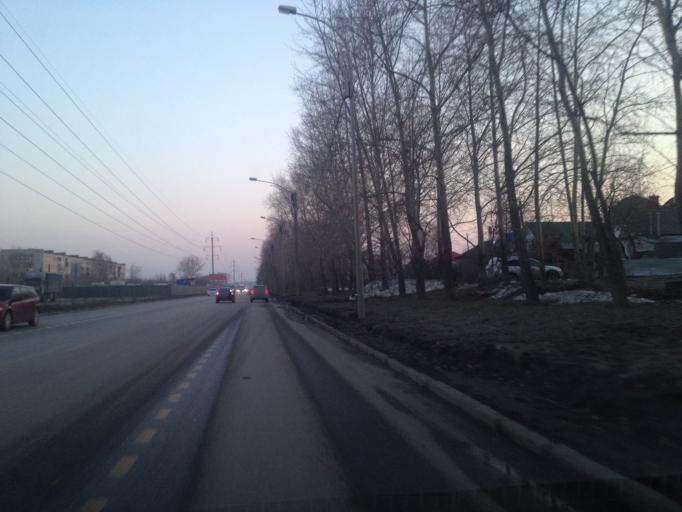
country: RU
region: Sverdlovsk
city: Sovkhoznyy
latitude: 56.7725
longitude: 60.5974
